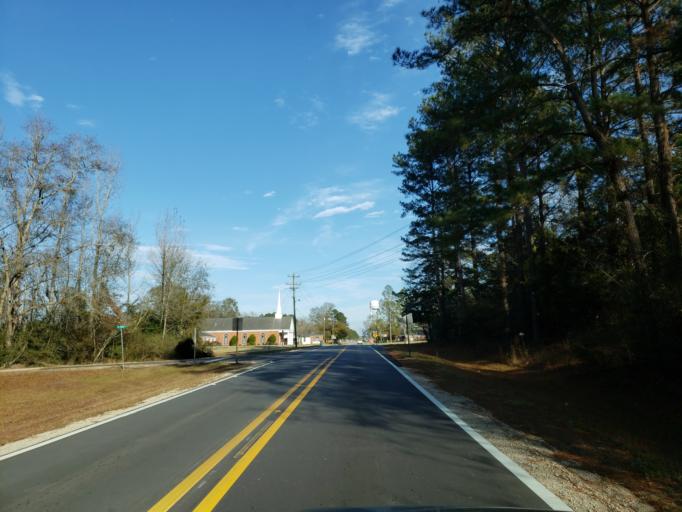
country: US
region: Mississippi
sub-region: Wayne County
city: Belmont
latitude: 31.4339
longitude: -88.4765
